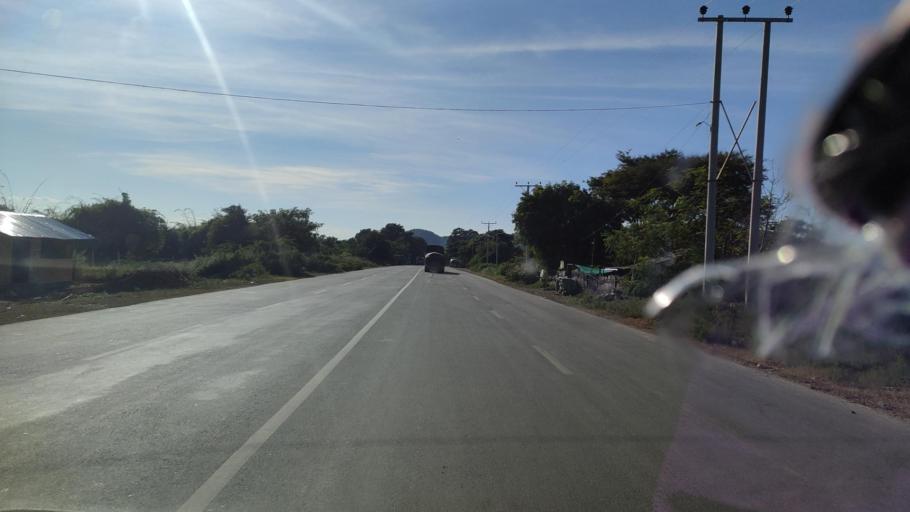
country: MM
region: Mandalay
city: Yamethin
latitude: 20.7544
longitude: 96.2520
